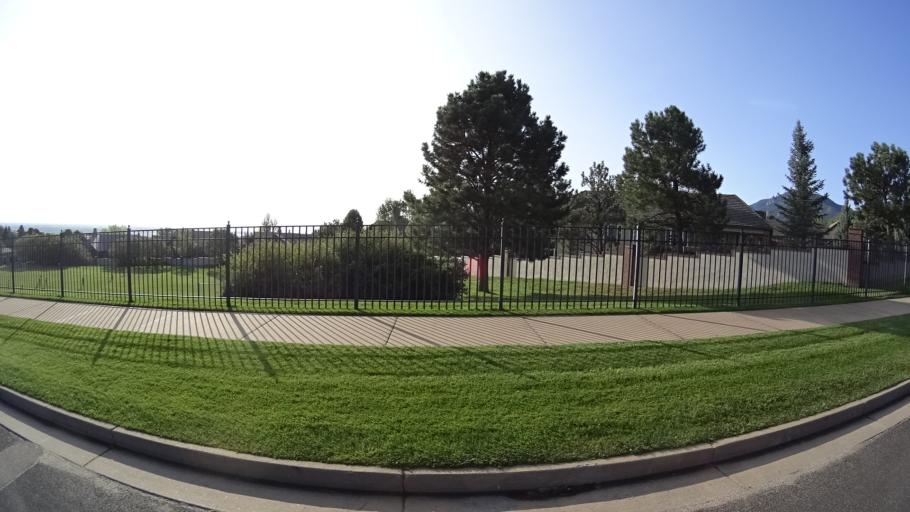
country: US
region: Colorado
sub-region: El Paso County
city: Colorado Springs
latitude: 38.8074
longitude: -104.8614
